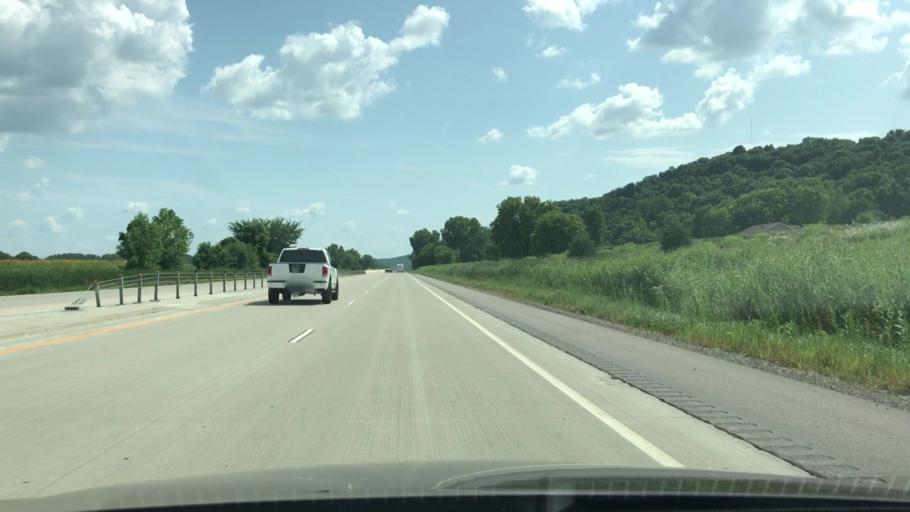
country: US
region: Minnesota
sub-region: Nicollet County
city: North Mankato
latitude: 44.2503
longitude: -94.0276
